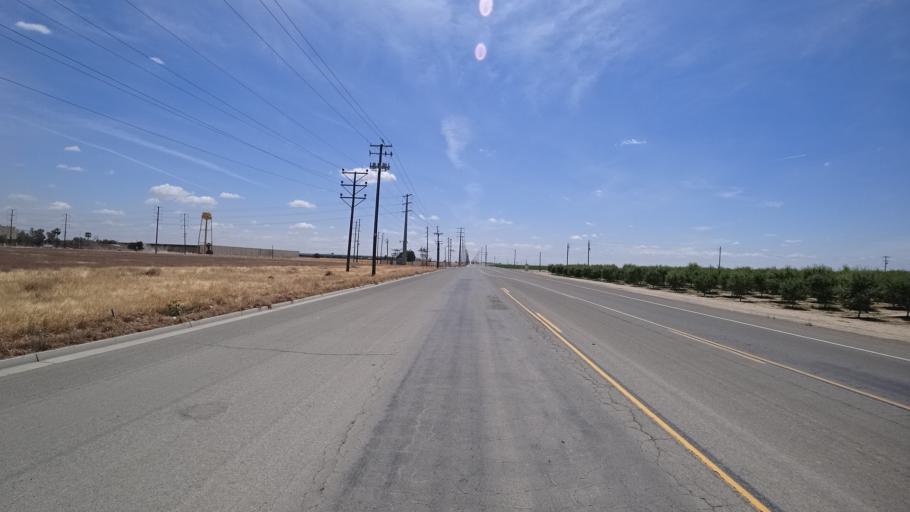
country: US
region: California
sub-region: Kings County
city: Home Garden
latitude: 36.2706
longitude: -119.6549
